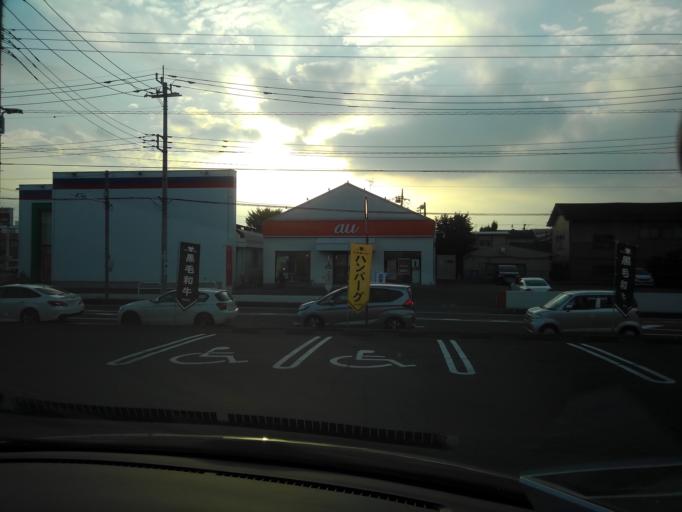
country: JP
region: Saitama
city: Tokorozawa
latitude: 35.7910
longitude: 139.4825
